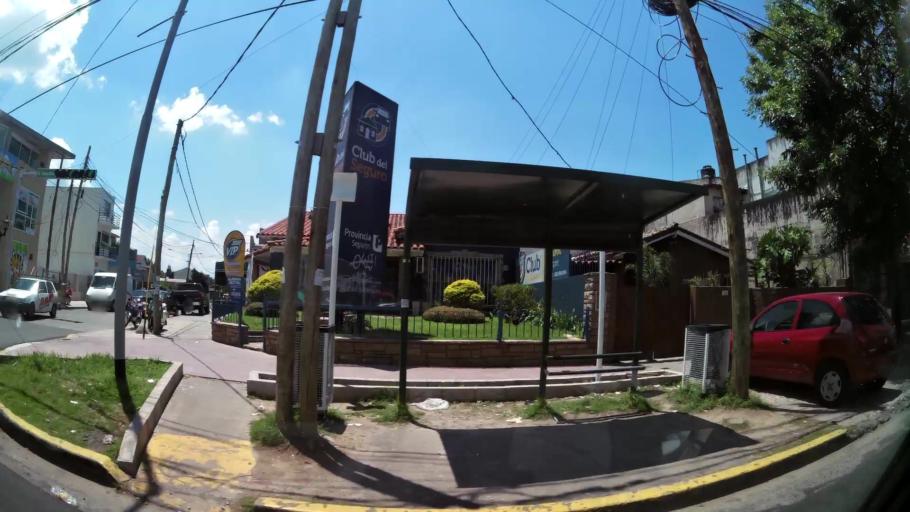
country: AR
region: Buenos Aires
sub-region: Partido de Tigre
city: Tigre
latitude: -34.4173
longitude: -58.5978
